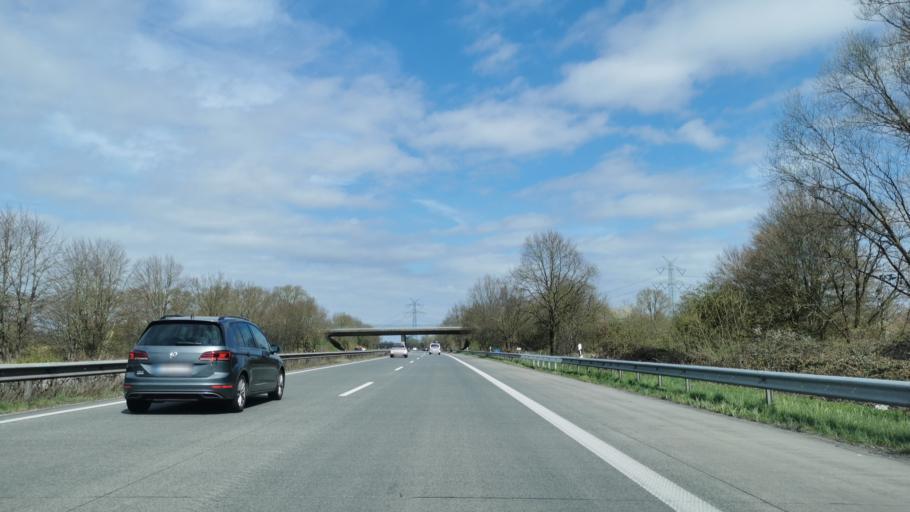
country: DE
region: Schleswig-Holstein
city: Kolln-Reisiek
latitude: 53.7759
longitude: 9.7066
